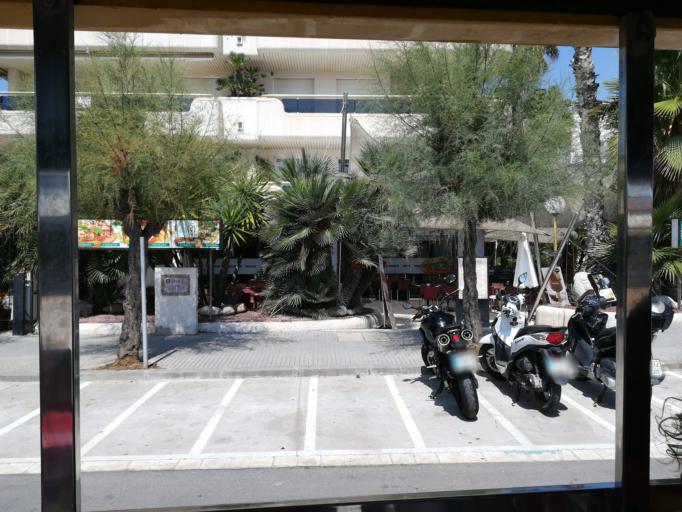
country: ES
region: Catalonia
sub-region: Provincia de Barcelona
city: Sitges
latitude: 41.2338
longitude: 1.8039
